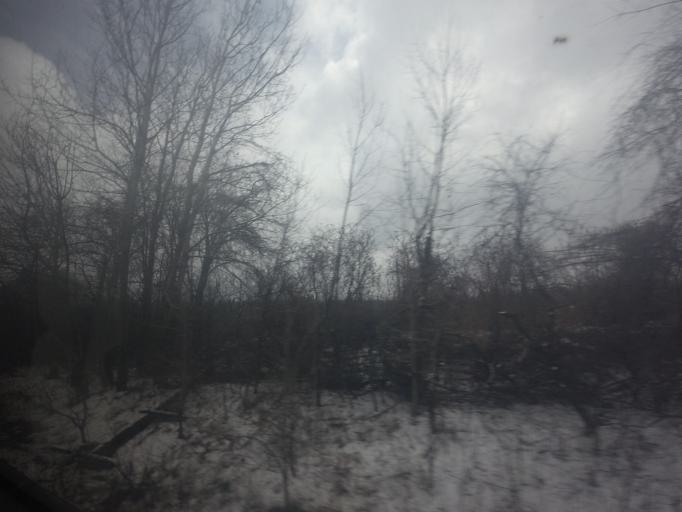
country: CA
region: Ontario
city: Cobourg
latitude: 43.9313
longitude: -78.4071
